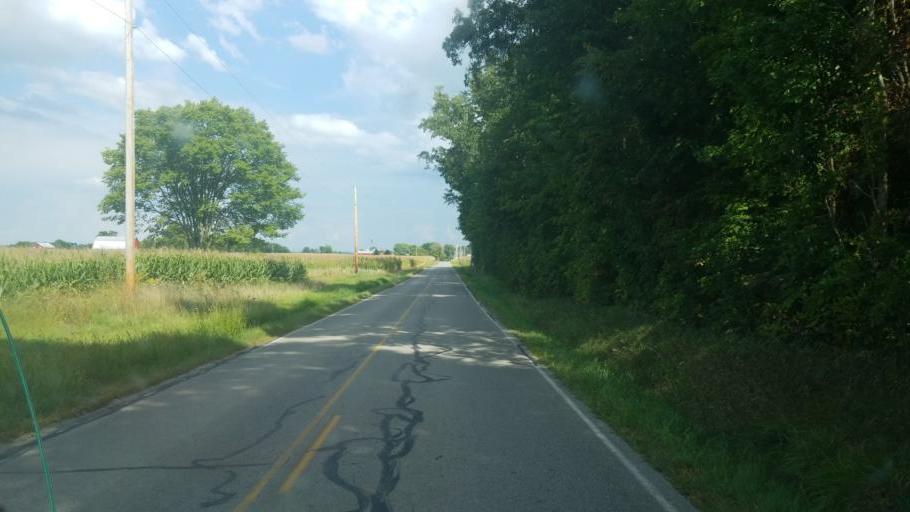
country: US
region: Ohio
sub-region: Huron County
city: Willard
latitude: 40.9819
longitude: -82.8025
